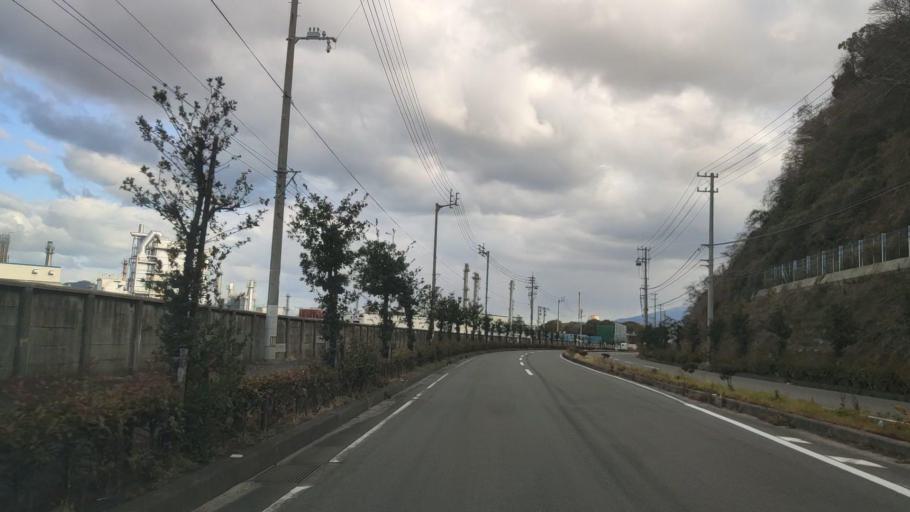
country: JP
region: Ehime
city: Masaki-cho
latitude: 33.8445
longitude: 132.7085
